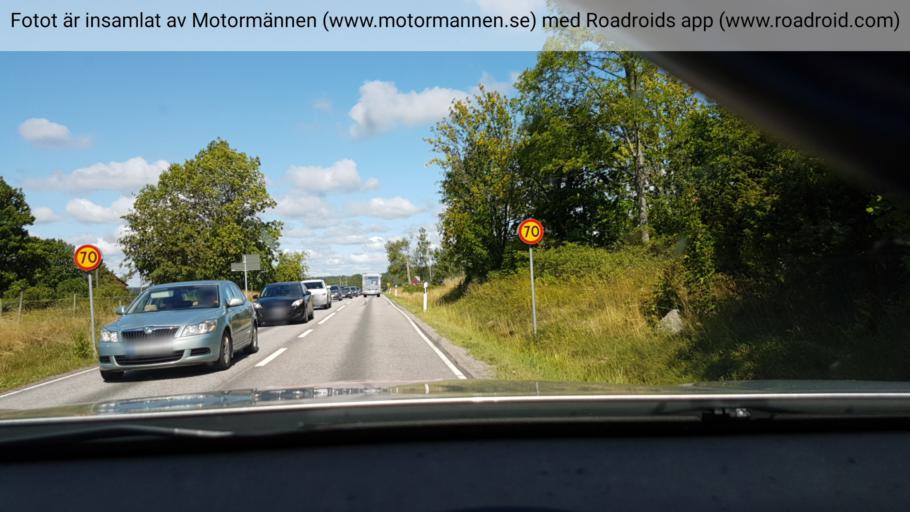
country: SE
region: Stockholm
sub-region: Norrtalje Kommun
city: Norrtalje
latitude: 59.7884
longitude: 18.6666
